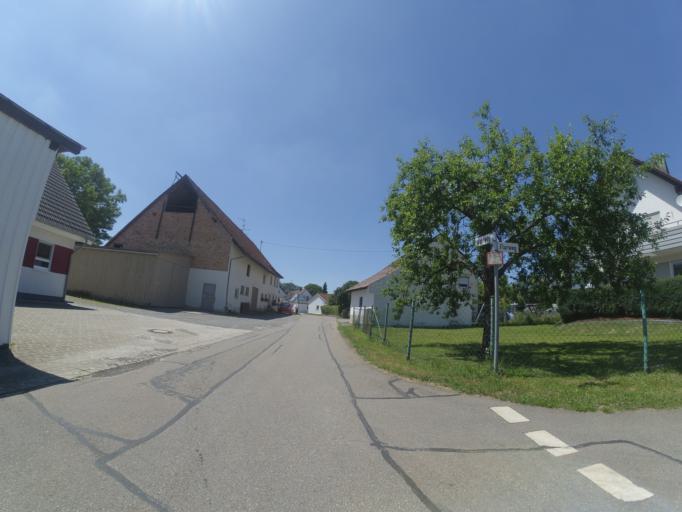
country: DE
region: Baden-Wuerttemberg
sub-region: Tuebingen Region
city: Aulendorf
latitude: 47.9254
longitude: 9.6872
